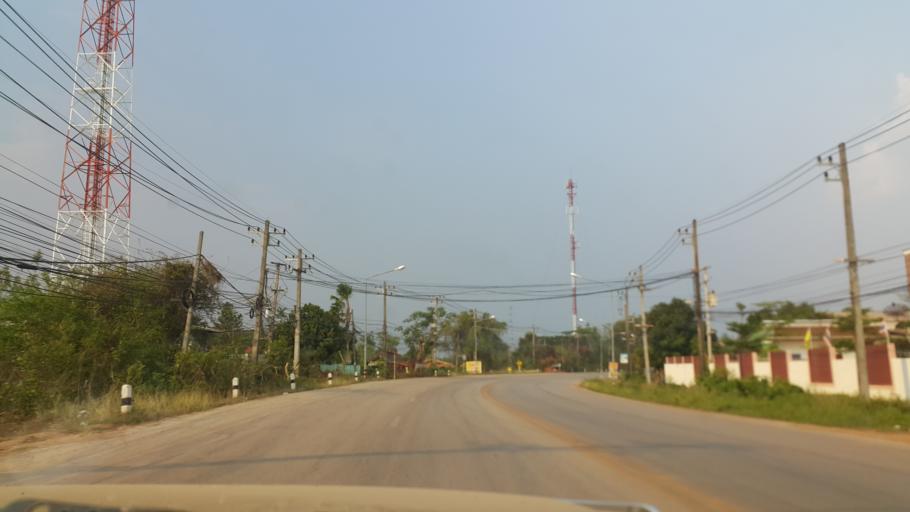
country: TH
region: Nakhon Phanom
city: That Phanom
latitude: 16.9540
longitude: 104.7224
